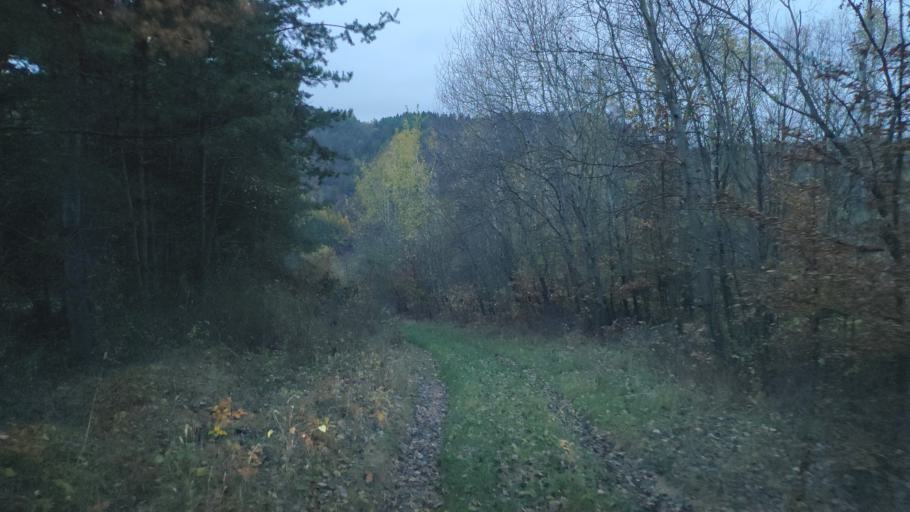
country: SK
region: Presovsky
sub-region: Okres Presov
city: Presov
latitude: 48.9396
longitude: 21.0842
